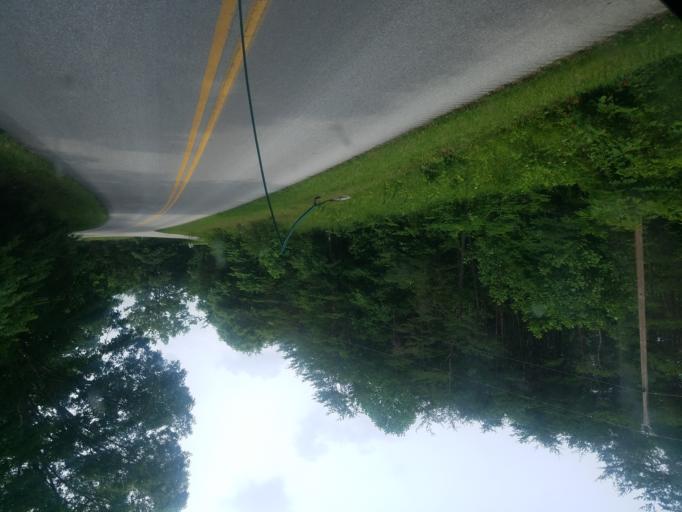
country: US
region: Kentucky
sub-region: Hart County
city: Munfordville
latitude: 37.2765
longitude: -86.0650
